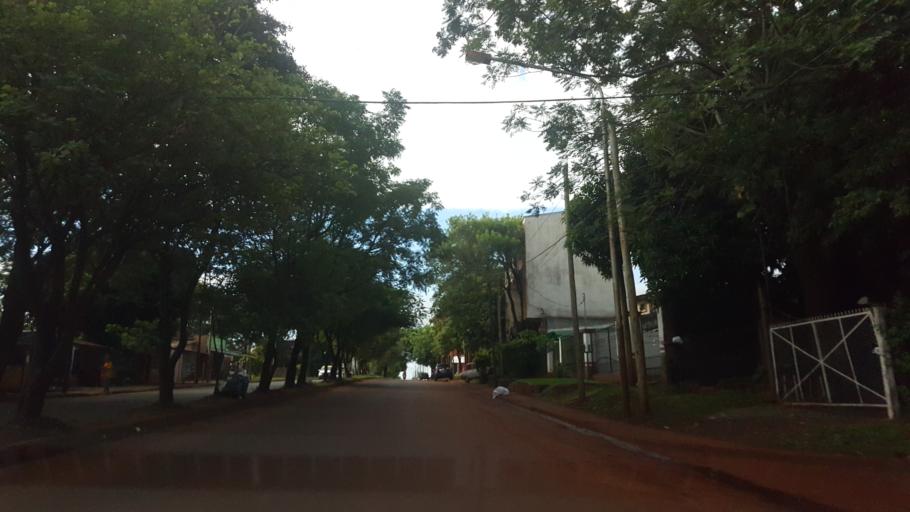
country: AR
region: Misiones
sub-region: Departamento de Capital
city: Posadas
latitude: -27.3891
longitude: -55.9347
